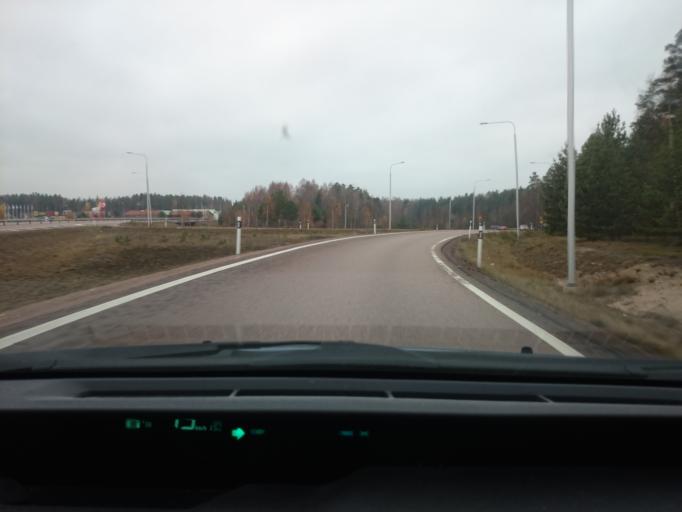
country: SE
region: Dalarna
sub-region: Avesta Kommun
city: Avesta
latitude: 60.1521
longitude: 16.2064
